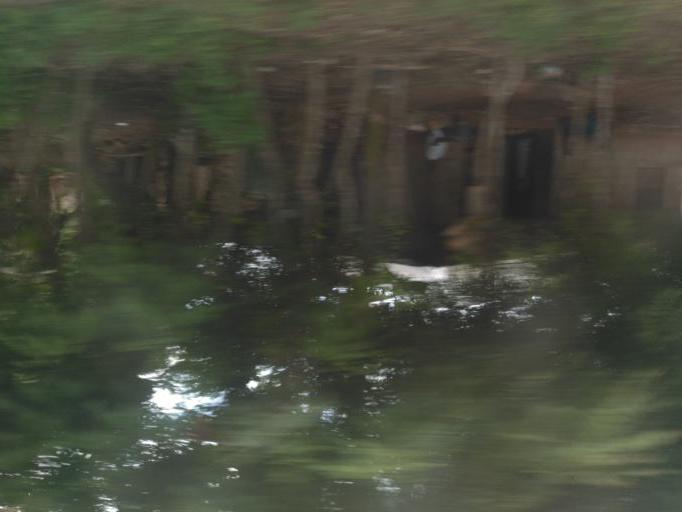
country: TZ
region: Zanzibar Urban/West
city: Zanzibar
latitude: -6.2686
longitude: 39.2656
